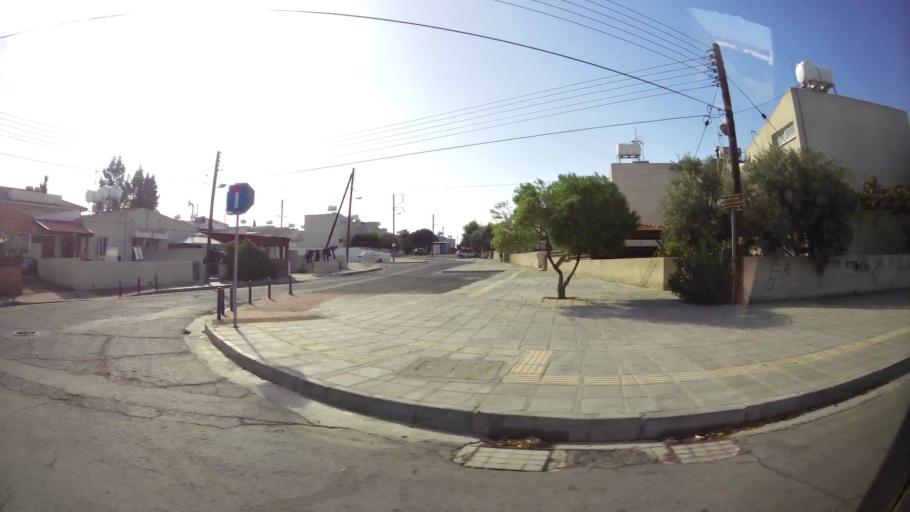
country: CY
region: Lefkosia
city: Nicosia
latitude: 35.1267
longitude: 33.3465
